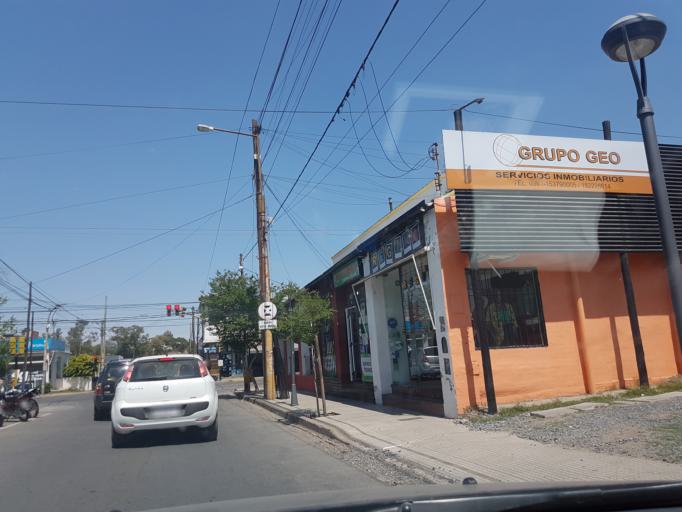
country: AR
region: Cordoba
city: Villa Allende
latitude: -31.2960
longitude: -64.2937
